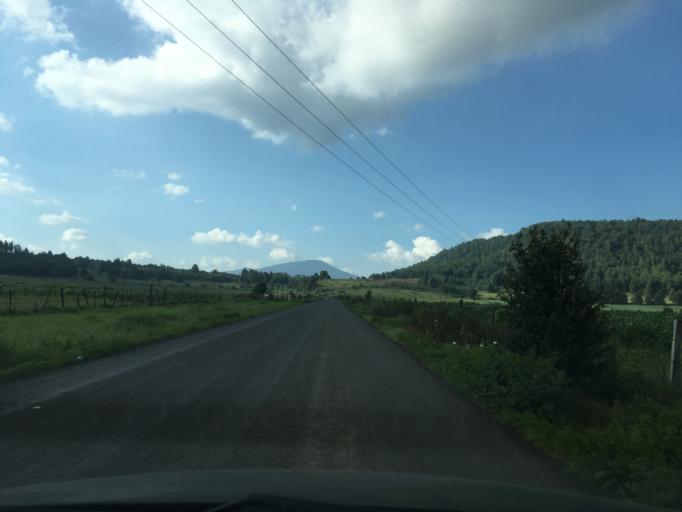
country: MX
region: Michoacan
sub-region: Nahuatzen
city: Sevina
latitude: 19.6226
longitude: -101.9283
